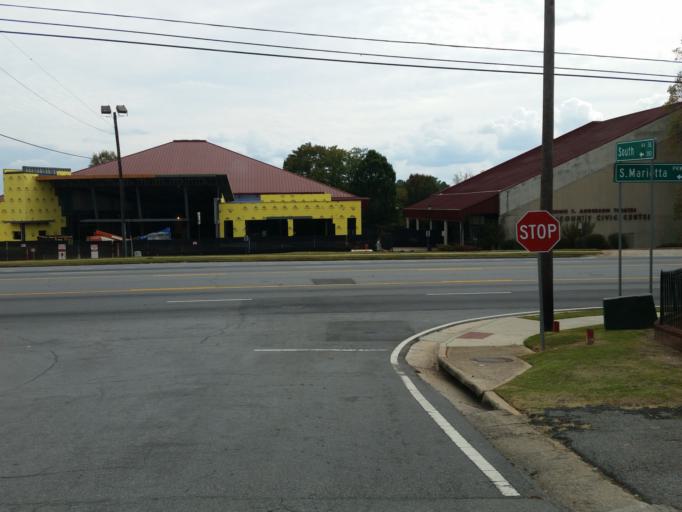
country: US
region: Georgia
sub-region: Cobb County
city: Marietta
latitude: 33.9437
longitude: -84.5370
